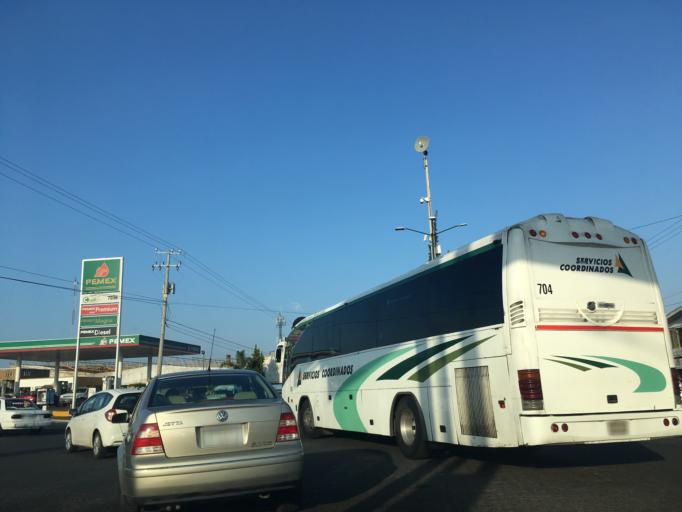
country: MX
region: Michoacan
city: Morelia
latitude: 19.7046
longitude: -101.2252
